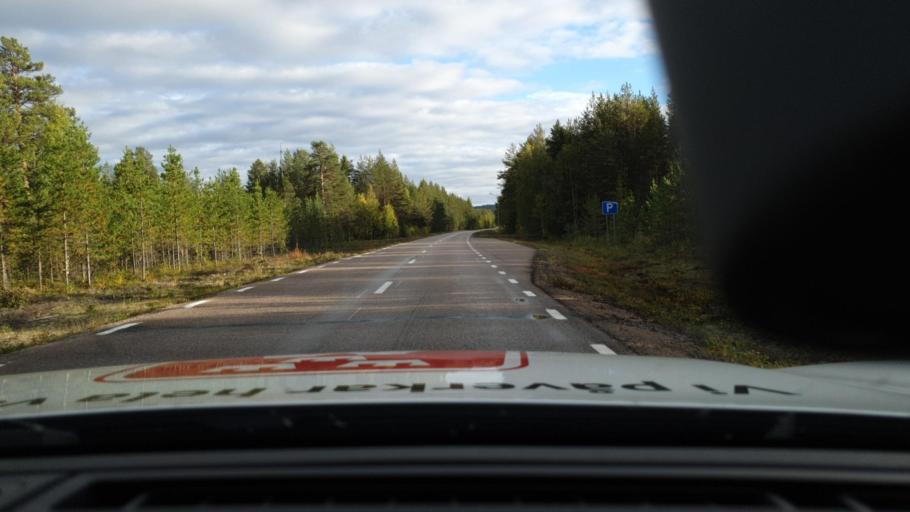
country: SE
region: Norrbotten
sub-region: Overkalix Kommun
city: OEverkalix
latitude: 66.6193
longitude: 22.7489
